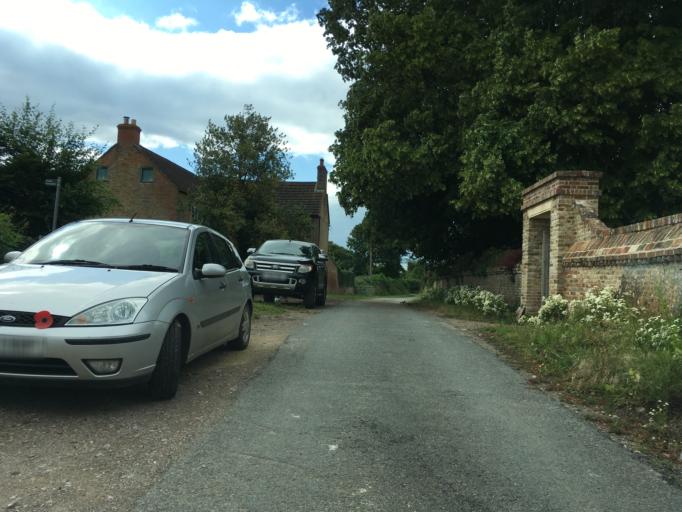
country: GB
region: England
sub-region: Gloucestershire
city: Cinderford
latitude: 51.8000
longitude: -2.4165
